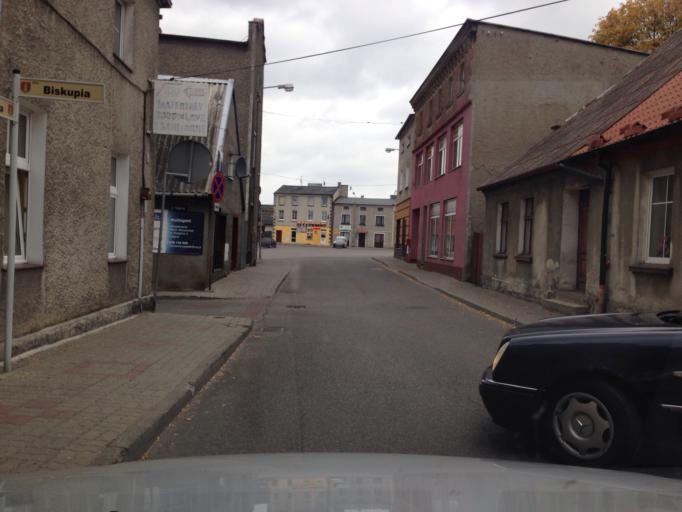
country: PL
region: Warmian-Masurian Voivodeship
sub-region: Powiat ilawski
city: Lubawa
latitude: 53.5047
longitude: 19.7514
